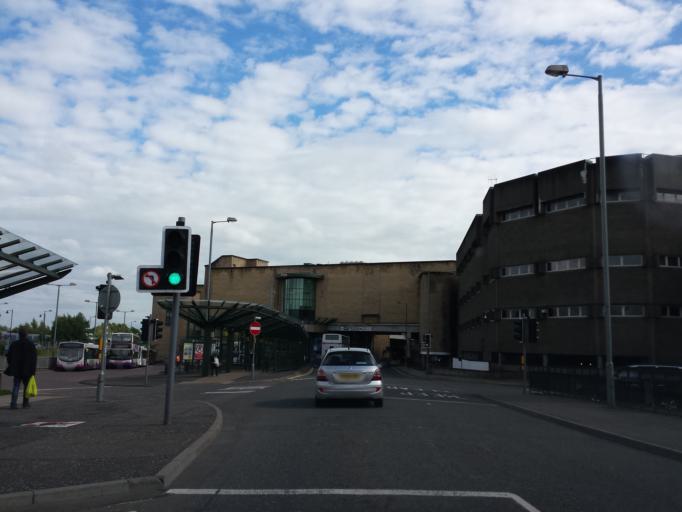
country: GB
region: Scotland
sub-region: Stirling
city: Stirling
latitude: 56.1188
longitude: -3.9351
